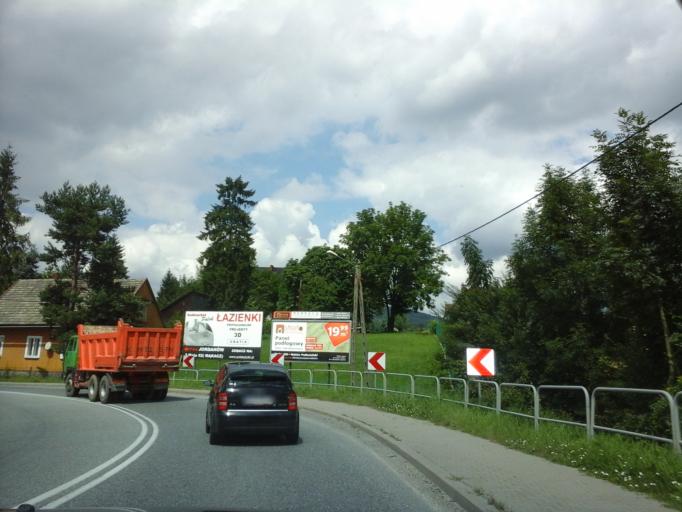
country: PL
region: Lesser Poland Voivodeship
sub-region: Powiat suski
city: Jordanow
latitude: 49.6516
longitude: 19.8247
